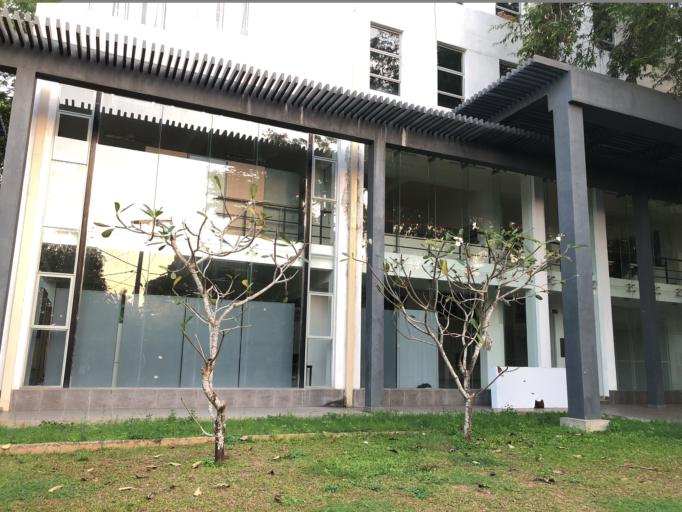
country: LK
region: Western
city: Moratuwa
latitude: 6.7986
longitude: 79.9016
